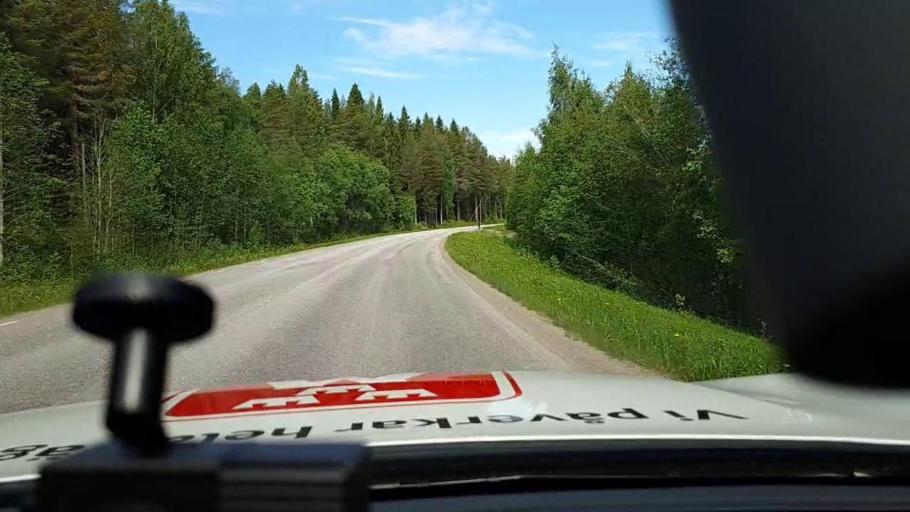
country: SE
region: Norrbotten
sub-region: Lulea Kommun
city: Gammelstad
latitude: 65.5897
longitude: 22.0024
